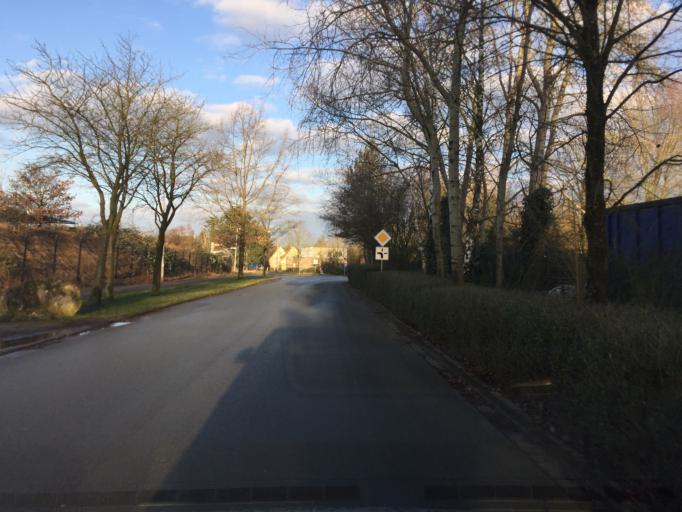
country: DE
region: Lower Saxony
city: Sulingen
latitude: 52.6915
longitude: 8.8157
